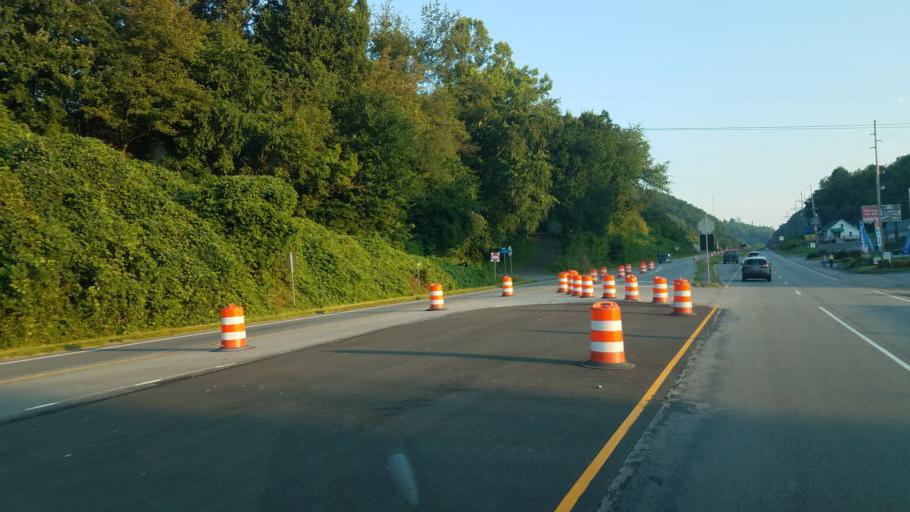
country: US
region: Virginia
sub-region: Scott County
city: Weber City
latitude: 36.6070
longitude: -82.5692
